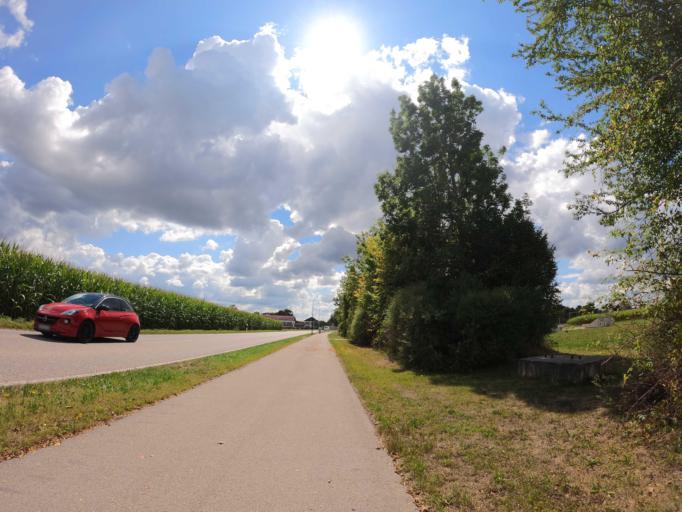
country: DE
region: Bavaria
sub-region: Upper Bavaria
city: Brunnthal
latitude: 48.0108
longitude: 11.6847
